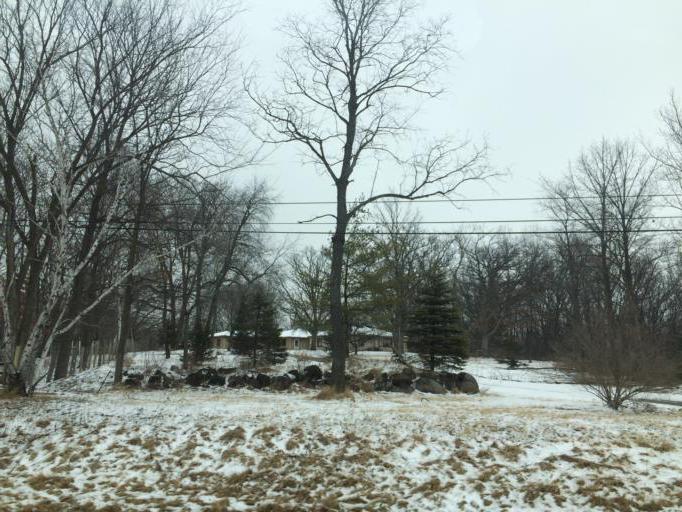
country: US
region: Illinois
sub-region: McHenry County
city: Harvard
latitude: 42.3824
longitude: -88.5870
